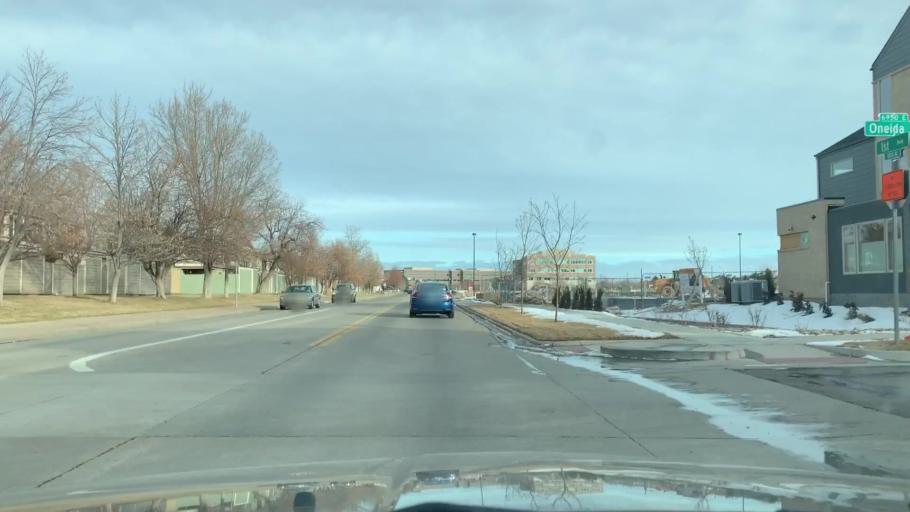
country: US
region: Colorado
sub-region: Arapahoe County
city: Glendale
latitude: 39.7183
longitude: -104.9078
